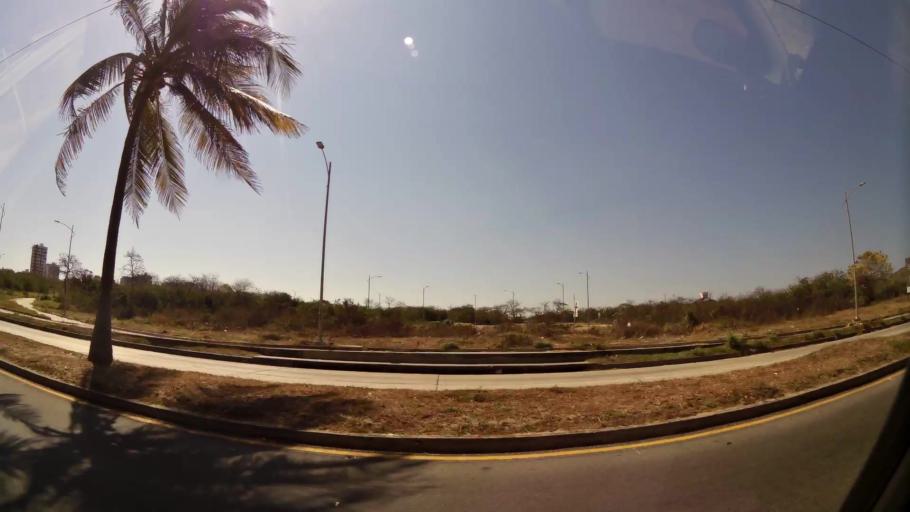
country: CO
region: Atlantico
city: Barranquilla
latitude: 11.0166
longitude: -74.8428
